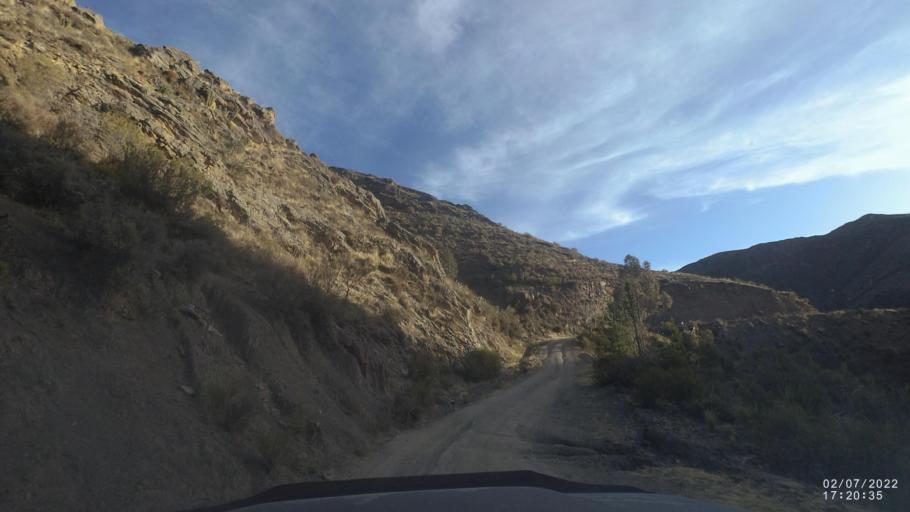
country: BO
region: Cochabamba
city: Irpa Irpa
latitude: -17.8783
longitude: -66.5957
